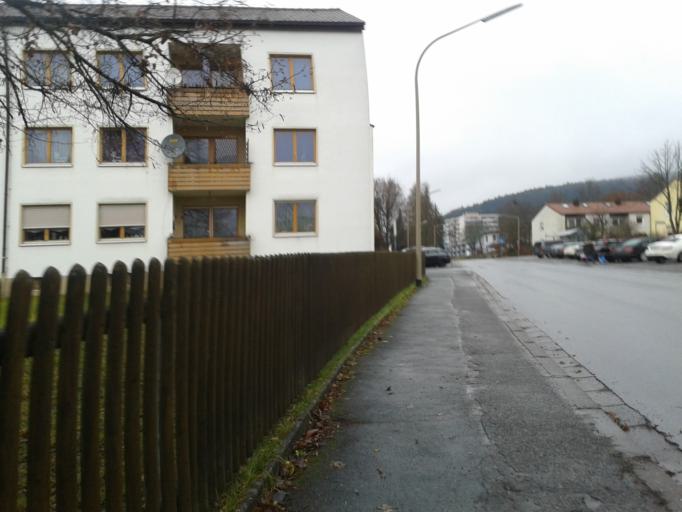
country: DE
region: Bavaria
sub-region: Upper Franconia
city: Kronach
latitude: 50.2360
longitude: 11.3400
